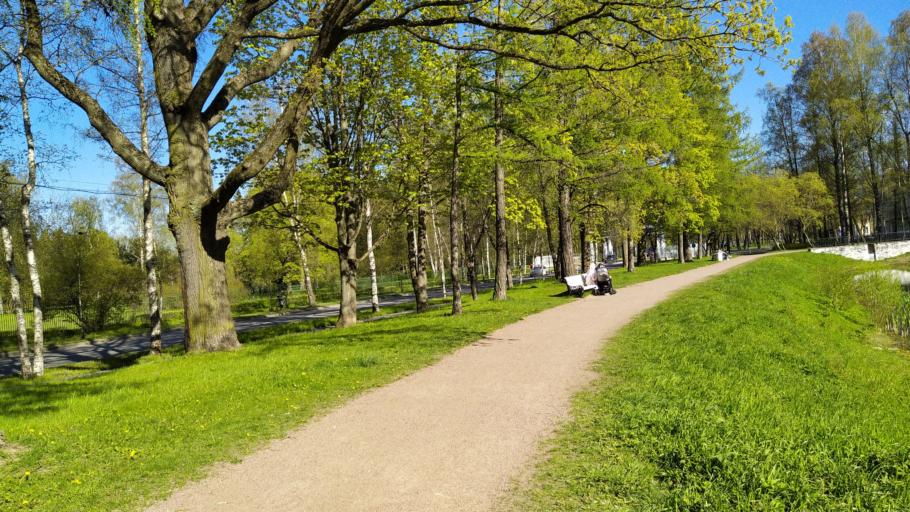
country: RU
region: St.-Petersburg
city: Pavlovsk
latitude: 59.6880
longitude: 30.4411
